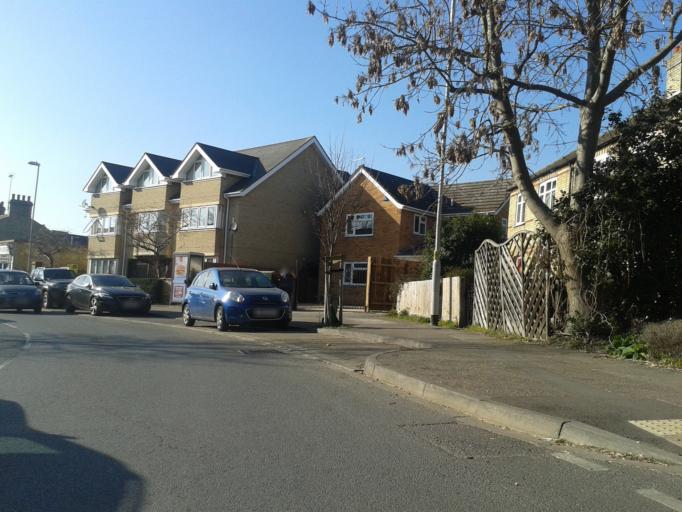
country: GB
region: England
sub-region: Cambridgeshire
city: Cambridge
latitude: 52.2180
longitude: 0.1413
